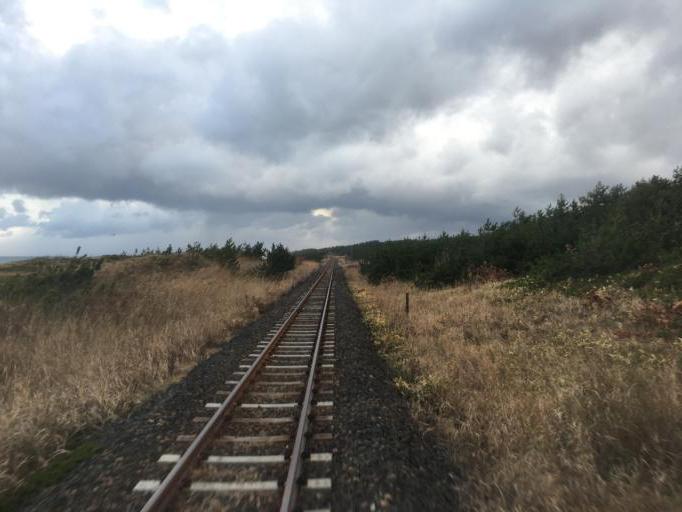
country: JP
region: Aomori
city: Mutsu
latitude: 40.9824
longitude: 141.2262
